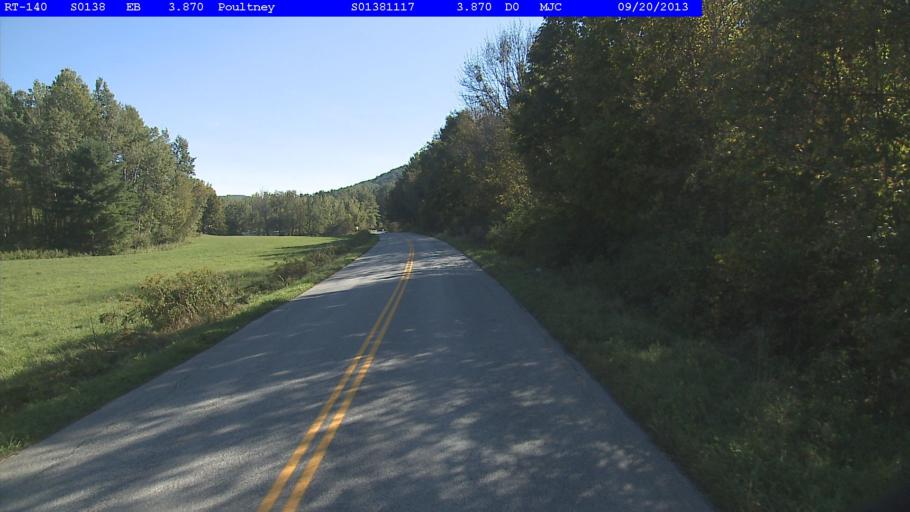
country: US
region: Vermont
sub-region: Rutland County
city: Poultney
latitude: 43.5101
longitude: -73.1776
